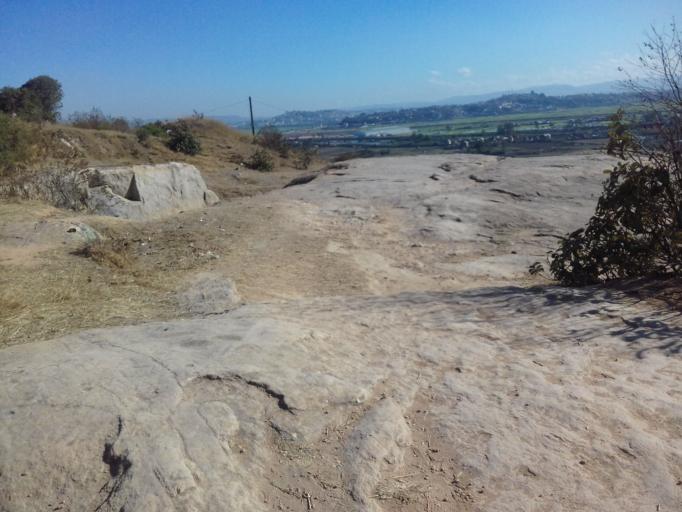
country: MG
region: Analamanga
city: Antananarivo
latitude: -18.8948
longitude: 47.4822
